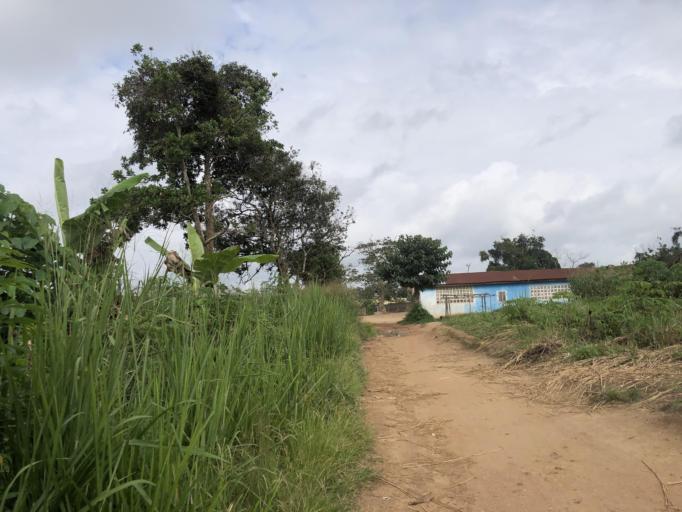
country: SL
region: Eastern Province
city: Kailahun
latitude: 8.2767
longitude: -10.5644
